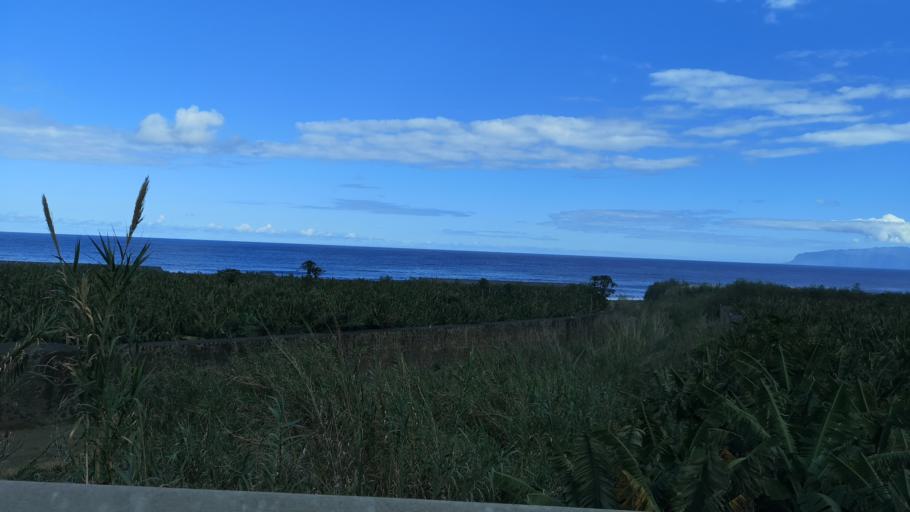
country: ES
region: Canary Islands
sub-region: Provincia de Santa Cruz de Tenerife
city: Hermigua
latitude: 28.1767
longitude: -17.1810
